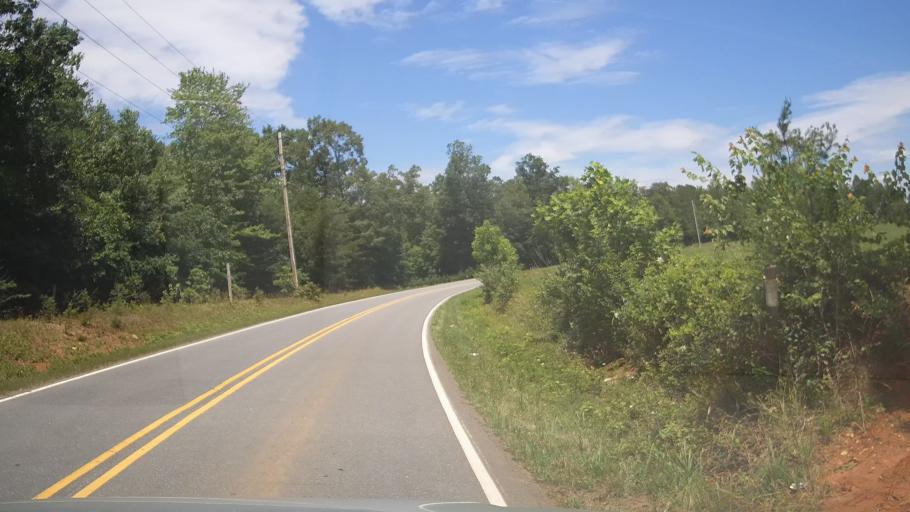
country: US
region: North Carolina
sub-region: Burke County
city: Glen Alpine
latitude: 35.6375
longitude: -81.7948
